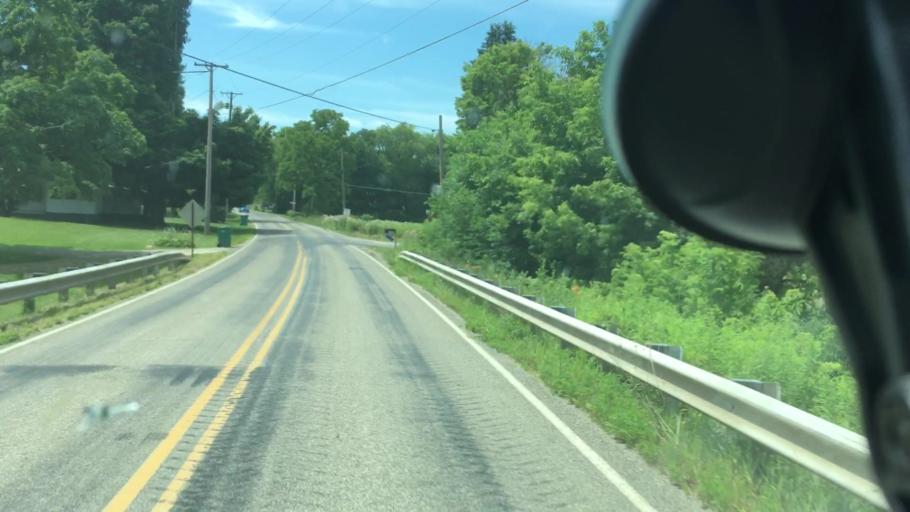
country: US
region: Pennsylvania
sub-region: Mercer County
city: Mercer
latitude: 41.2255
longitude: -80.2177
